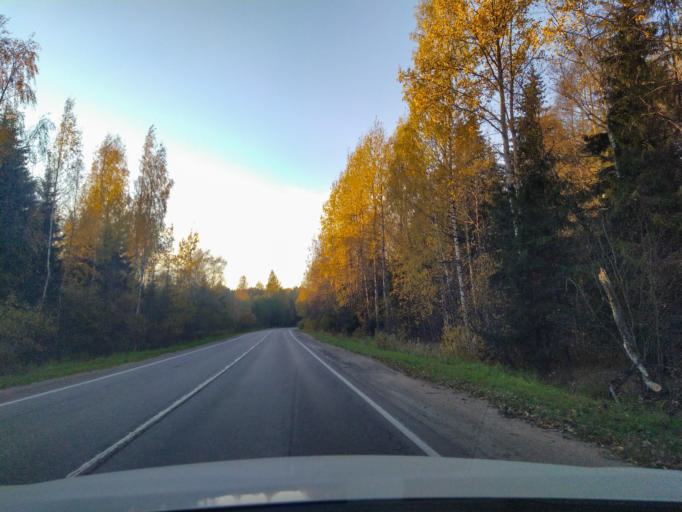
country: RU
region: Leningrad
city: Kobrinskoye
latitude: 59.4068
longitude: 30.1268
